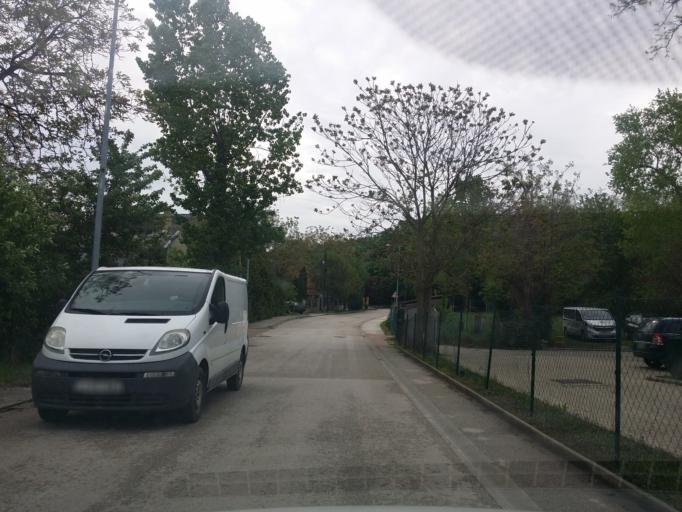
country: HU
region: Pest
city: Biatorbagy
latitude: 47.4725
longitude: 18.8288
